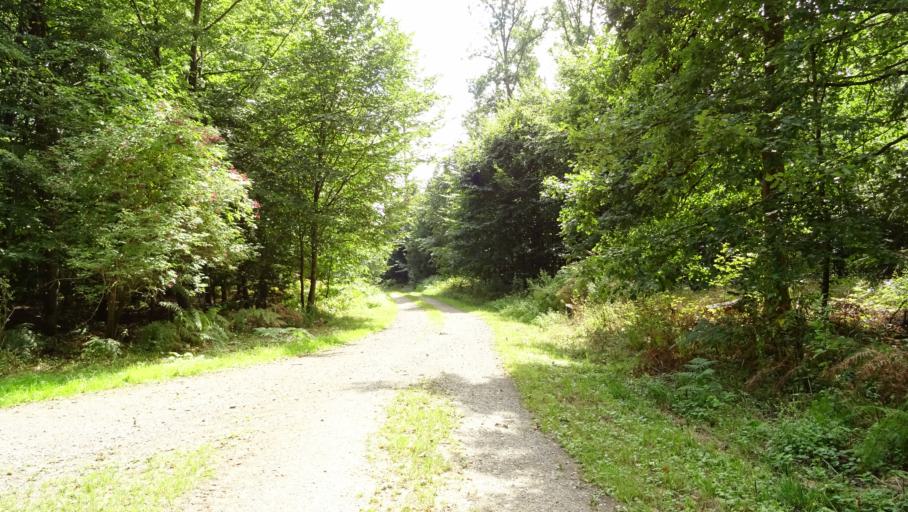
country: DE
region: Baden-Wuerttemberg
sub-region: Karlsruhe Region
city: Fahrenbach
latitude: 49.4217
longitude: 9.1334
